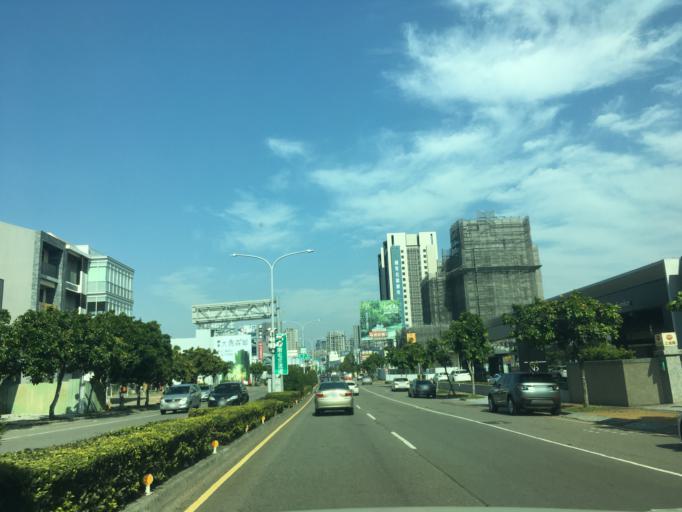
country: TW
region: Taiwan
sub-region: Taichung City
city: Taichung
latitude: 24.1453
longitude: 120.6239
